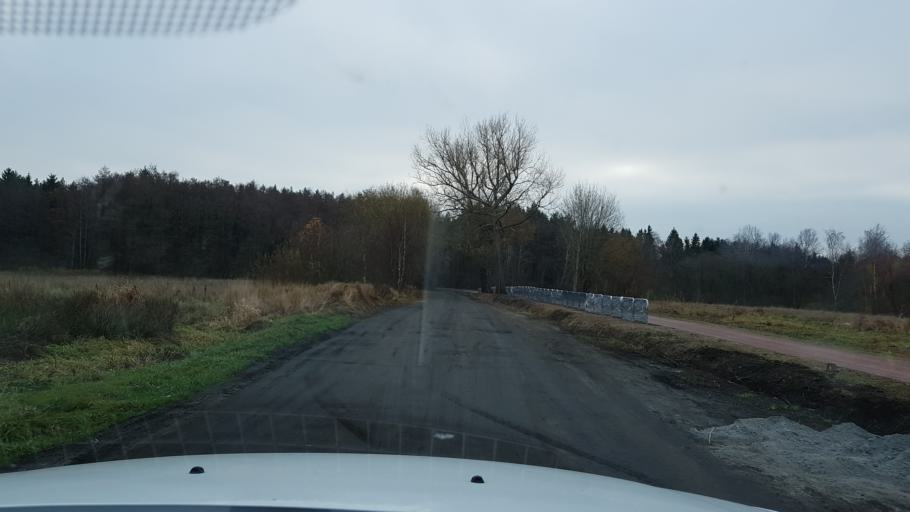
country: PL
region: West Pomeranian Voivodeship
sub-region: Powiat kolobrzeski
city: Grzybowo
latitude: 54.1361
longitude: 15.5139
